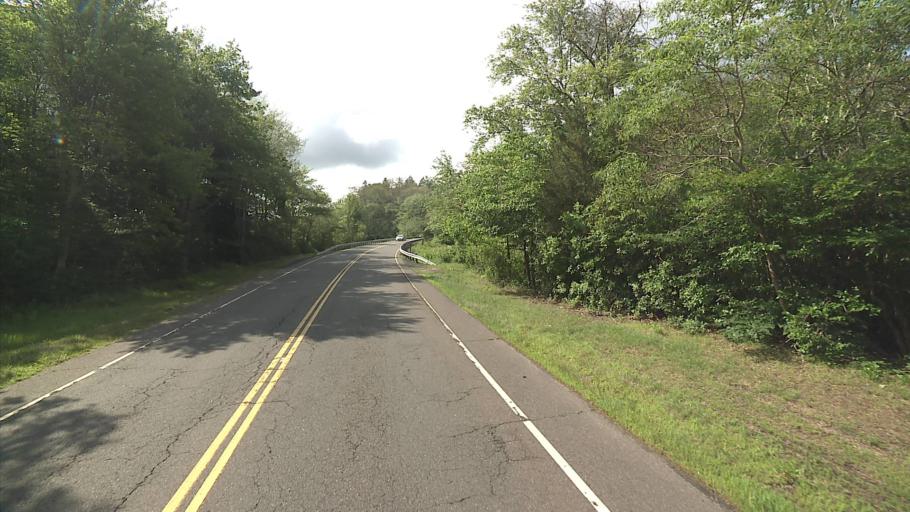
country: US
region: Connecticut
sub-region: Middlesex County
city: Deep River Center
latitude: 41.3423
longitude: -72.4945
